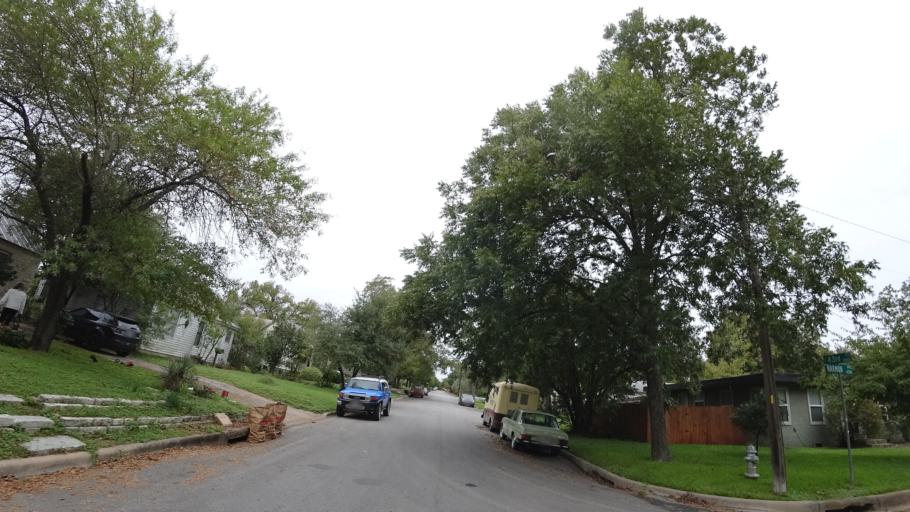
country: US
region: Texas
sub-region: Travis County
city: Austin
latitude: 30.3012
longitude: -97.7179
